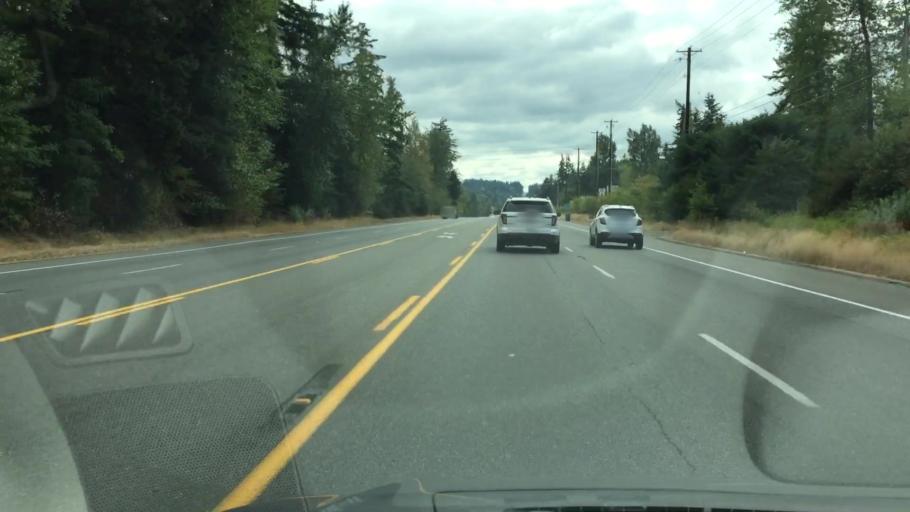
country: US
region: Washington
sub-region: Pierce County
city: Graham
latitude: 47.0666
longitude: -122.2948
